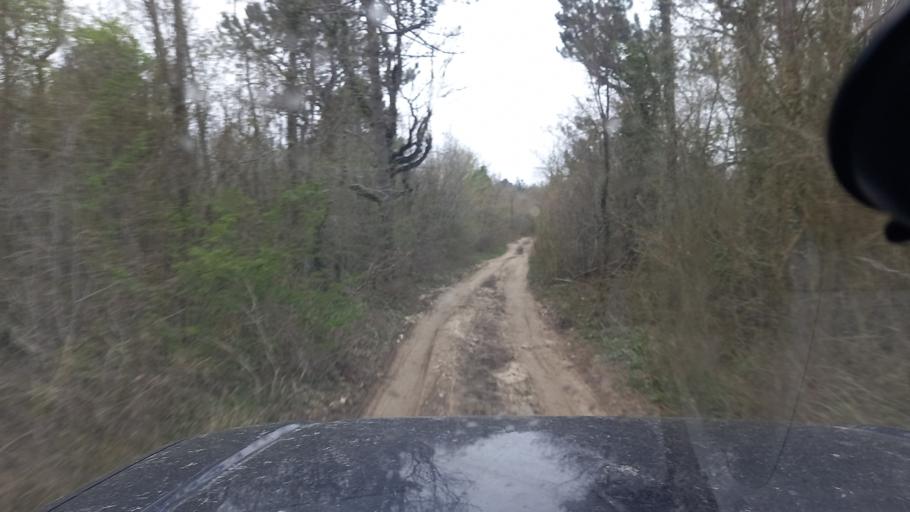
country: RU
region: Krasnodarskiy
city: Dzhubga
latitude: 44.3148
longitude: 38.6790
